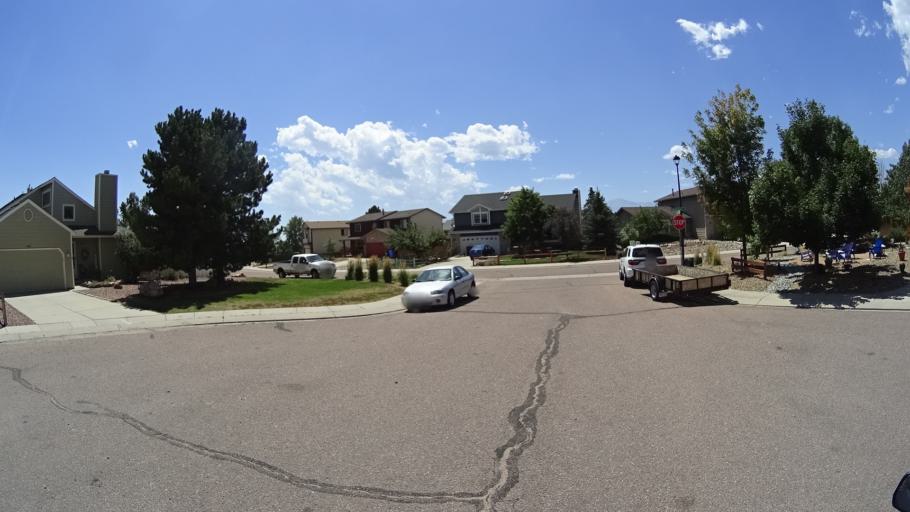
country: US
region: Colorado
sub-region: El Paso County
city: Black Forest
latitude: 38.9503
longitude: -104.7444
